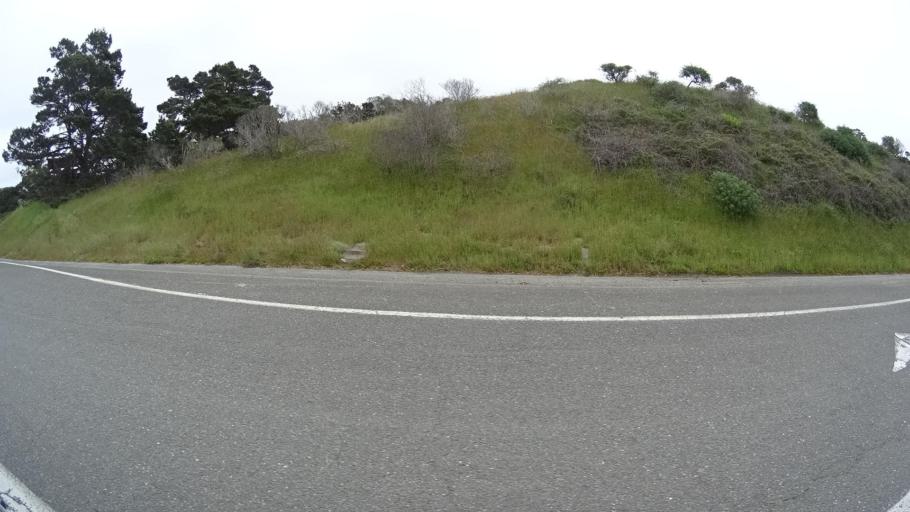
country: US
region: California
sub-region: Humboldt County
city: Eureka
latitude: 40.8230
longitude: -124.1822
